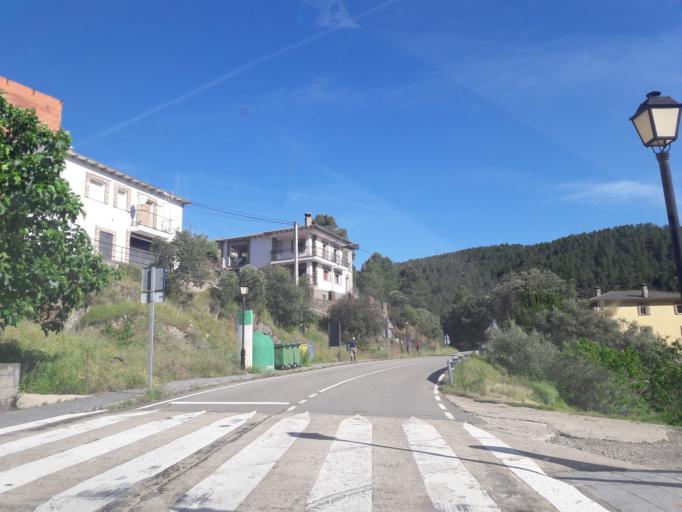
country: ES
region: Castille and Leon
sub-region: Provincia de Salamanca
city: Herguijuela de la Sierra
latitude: 40.4052
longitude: -6.0850
